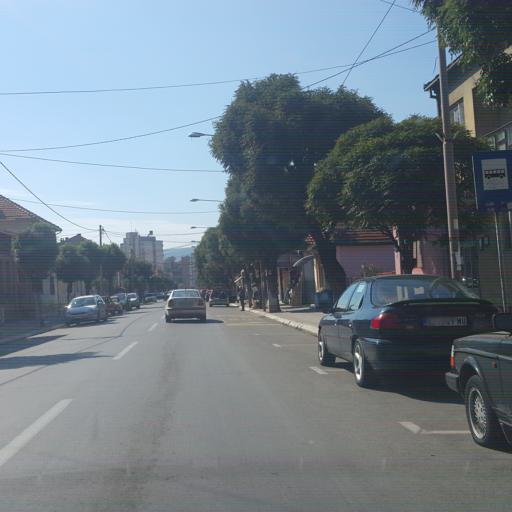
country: RS
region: Central Serbia
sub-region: Zajecarski Okrug
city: Knjazevac
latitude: 43.5709
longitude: 22.2624
